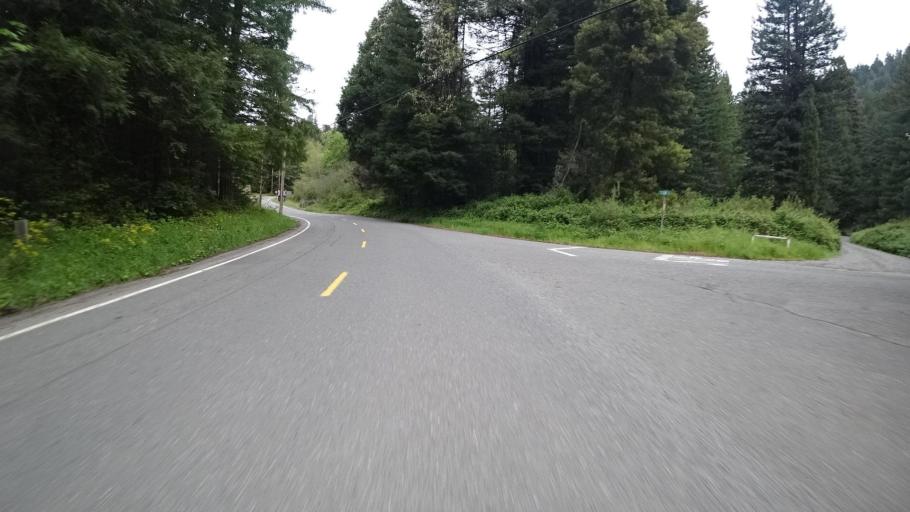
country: US
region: California
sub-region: Humboldt County
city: Redway
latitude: 40.3248
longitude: -123.9247
